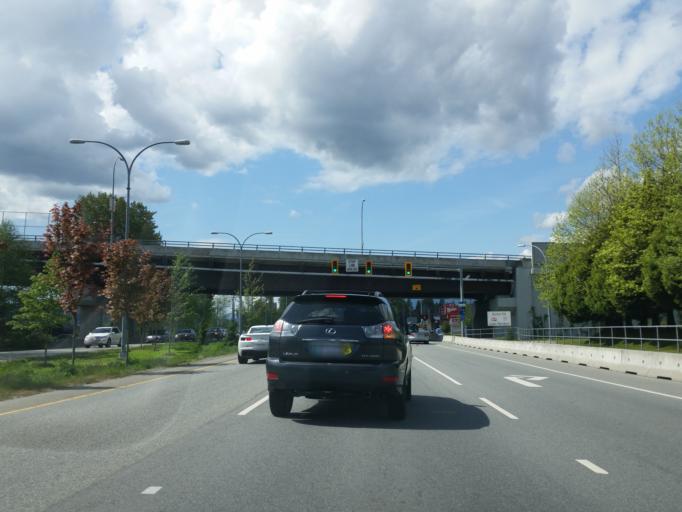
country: CA
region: British Columbia
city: Coquitlam
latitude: 49.2589
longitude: -122.7554
